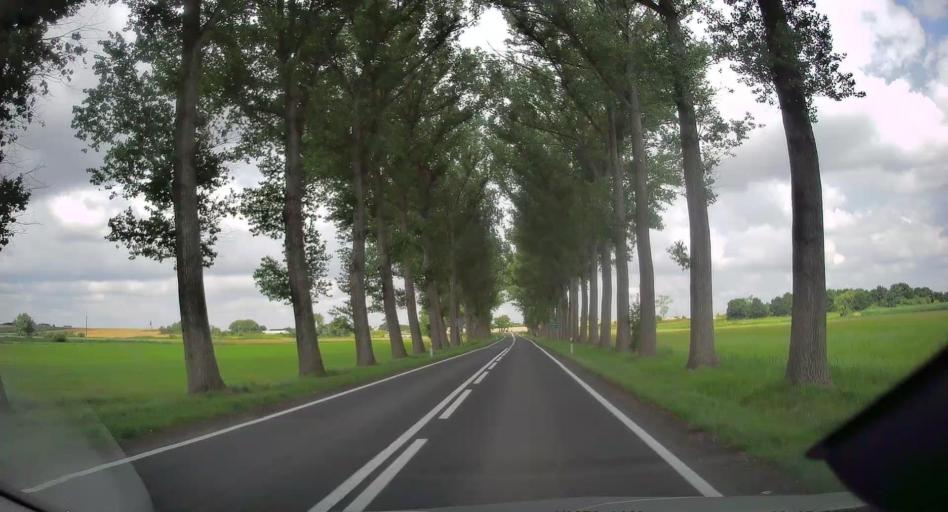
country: PL
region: Opole Voivodeship
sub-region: Powiat prudnicki
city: Twardawa
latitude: 50.3385
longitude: 17.9576
